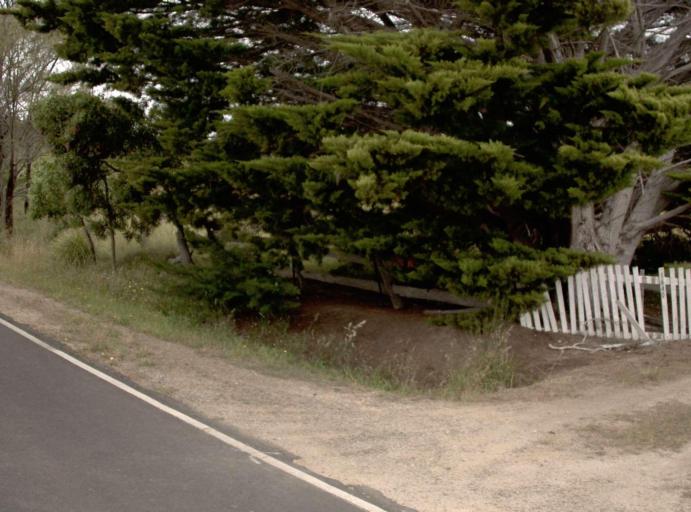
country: AU
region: Victoria
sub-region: Latrobe
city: Traralgon
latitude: -38.4857
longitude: 146.8202
